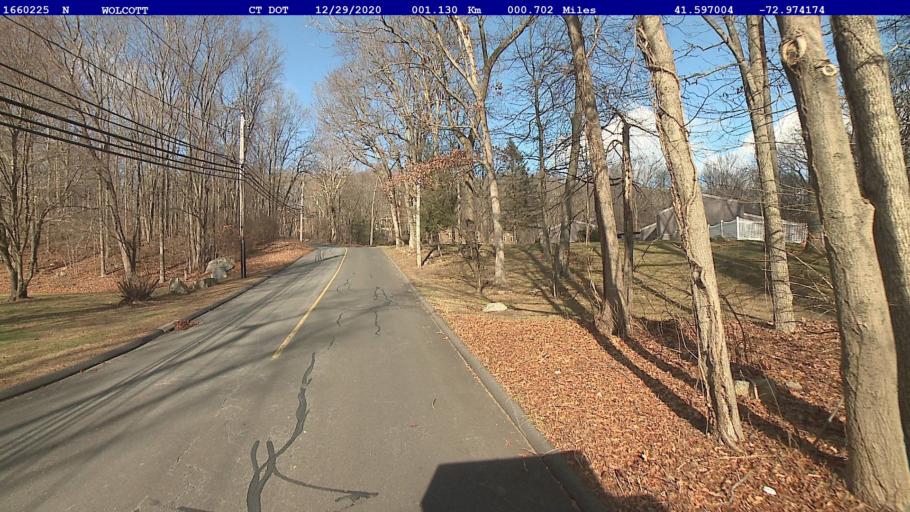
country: US
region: Connecticut
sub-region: New Haven County
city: Wolcott
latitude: 41.5970
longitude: -72.9742
